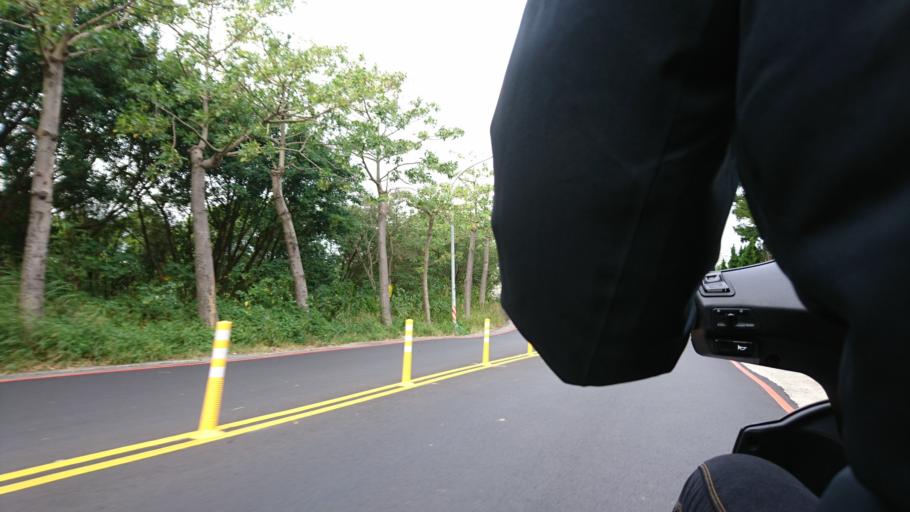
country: TW
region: Taiwan
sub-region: Hsinchu
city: Hsinchu
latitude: 24.7910
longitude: 120.9572
